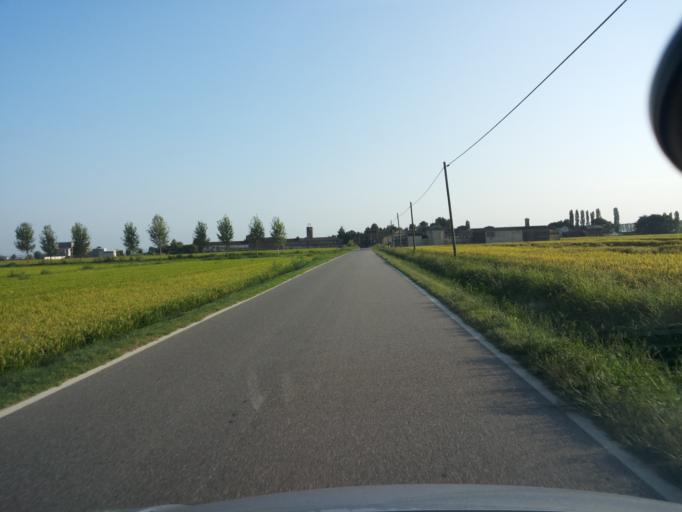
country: IT
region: Piedmont
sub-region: Provincia di Vercelli
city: Sali Vercellese
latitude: 45.3143
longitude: 8.3310
